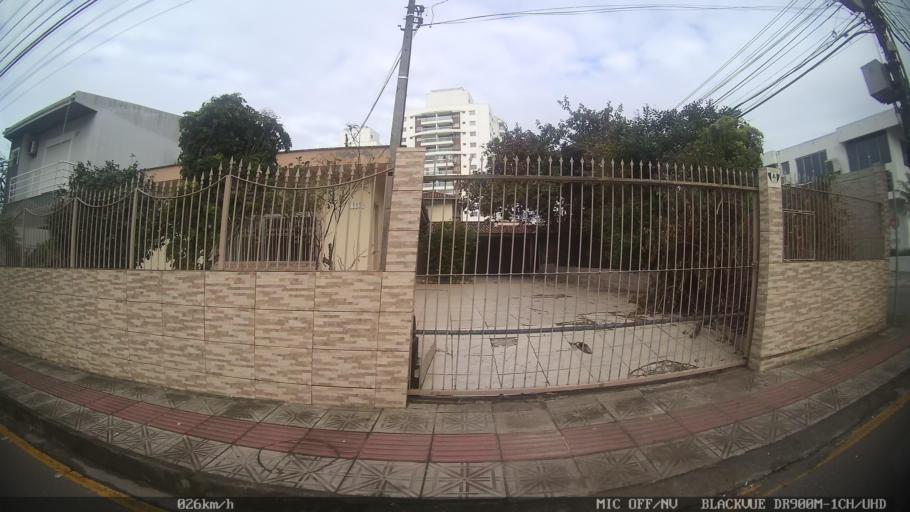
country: BR
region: Santa Catarina
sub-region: Sao Jose
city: Campinas
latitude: -27.5708
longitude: -48.6093
